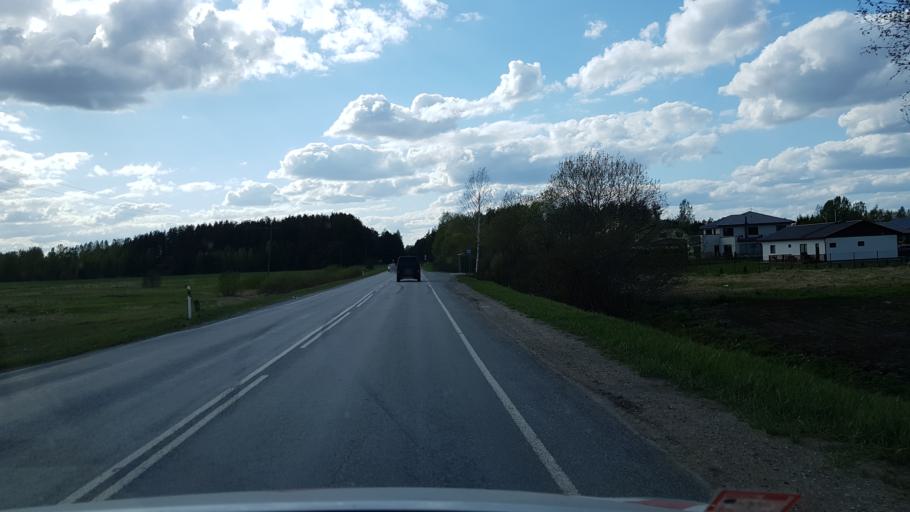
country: EE
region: Tartu
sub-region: UElenurme vald
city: Ulenurme
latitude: 58.3255
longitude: 26.7877
